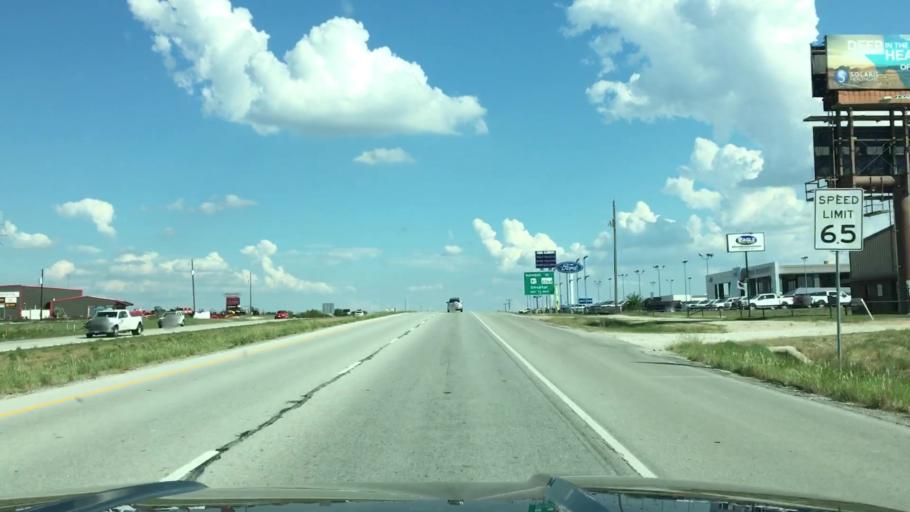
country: US
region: Texas
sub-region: Wise County
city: Decatur
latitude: 33.2117
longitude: -97.5788
